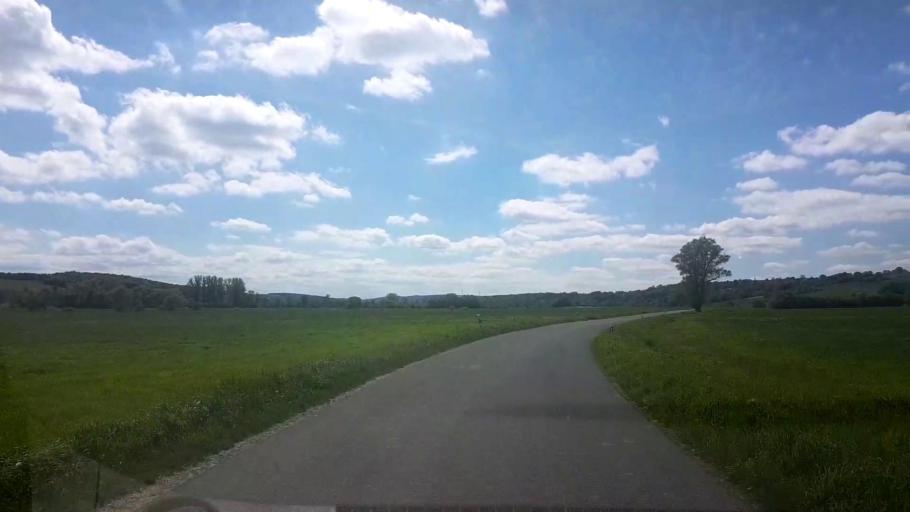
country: DE
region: Bavaria
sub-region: Upper Franconia
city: Grossheirath
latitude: 50.1607
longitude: 10.9267
